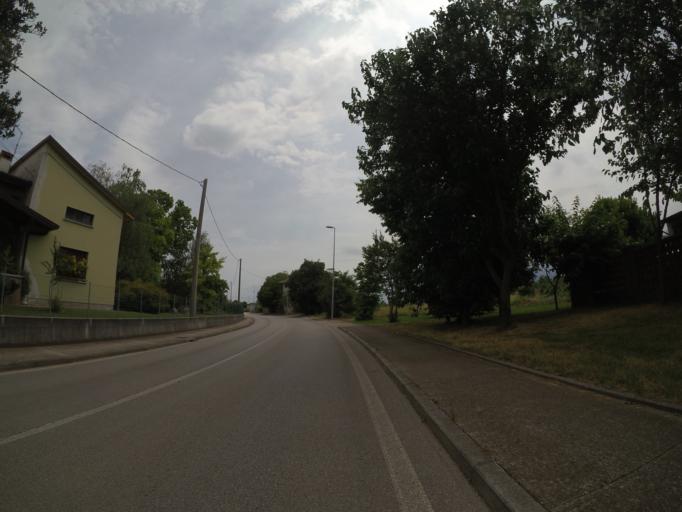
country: IT
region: Friuli Venezia Giulia
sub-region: Provincia di Udine
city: Sedegliano
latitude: 46.0101
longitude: 12.9787
